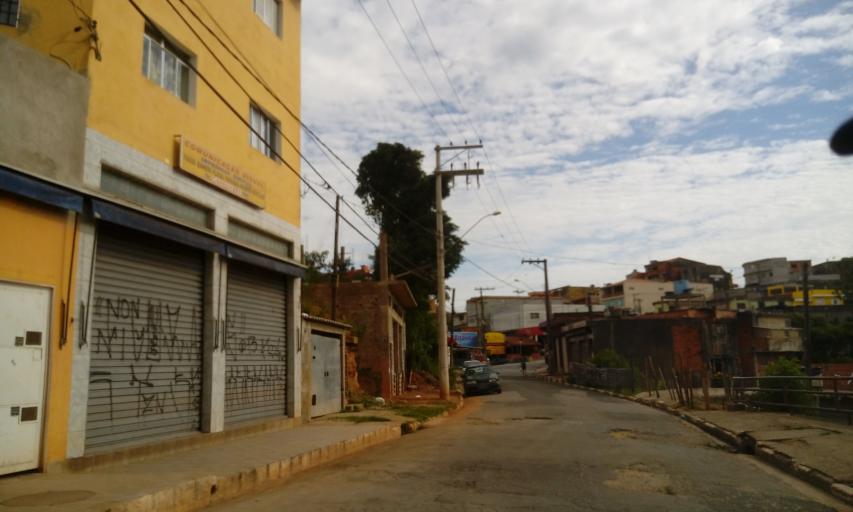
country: BR
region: Sao Paulo
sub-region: Francisco Morato
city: Francisco Morato
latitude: -23.2649
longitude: -46.7446
